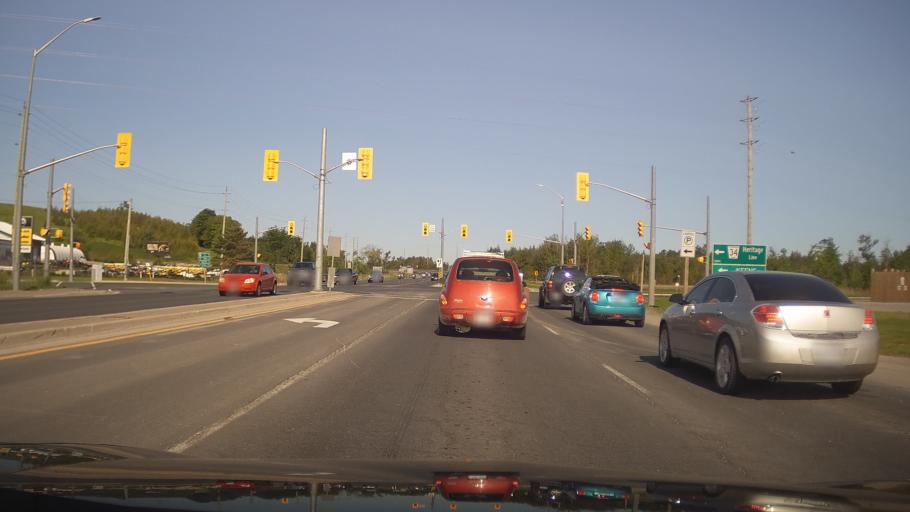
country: CA
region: Ontario
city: Peterborough
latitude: 44.3169
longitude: -78.1984
